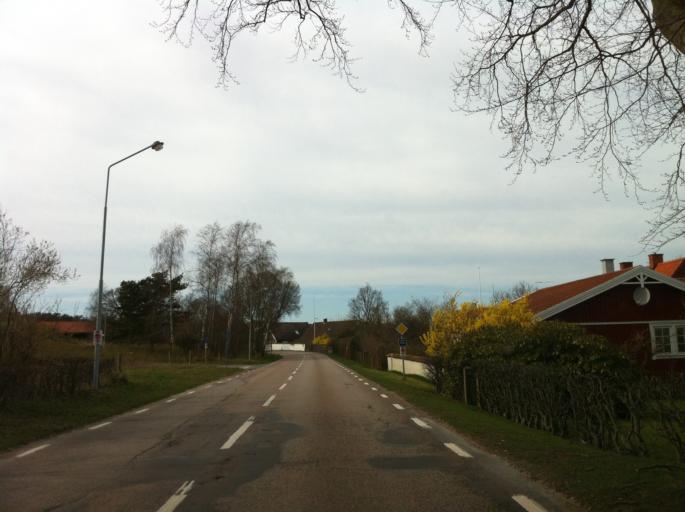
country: SE
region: Skane
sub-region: Hoganas Kommun
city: Hoganas
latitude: 56.2509
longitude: 12.6609
